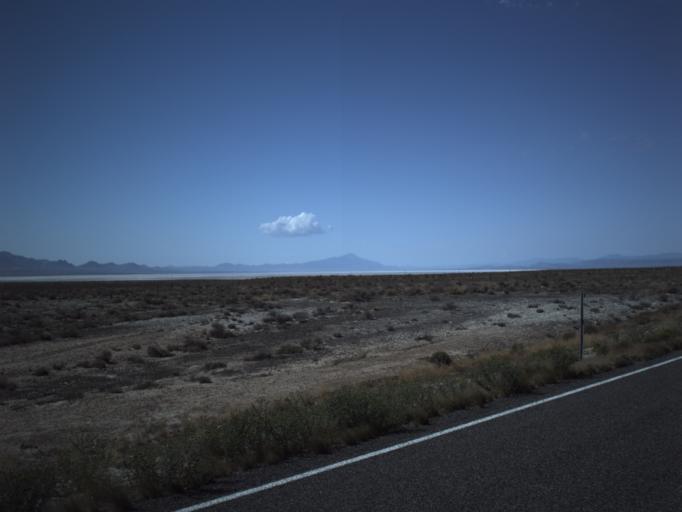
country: US
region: Utah
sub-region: Millard County
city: Delta
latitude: 39.1646
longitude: -113.0447
